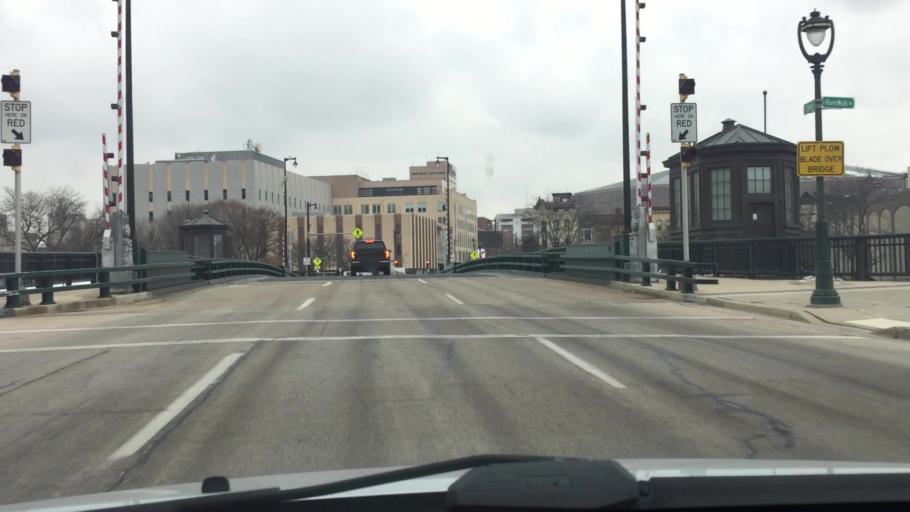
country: US
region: Wisconsin
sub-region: Milwaukee County
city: Milwaukee
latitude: 43.0431
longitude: -87.9126
